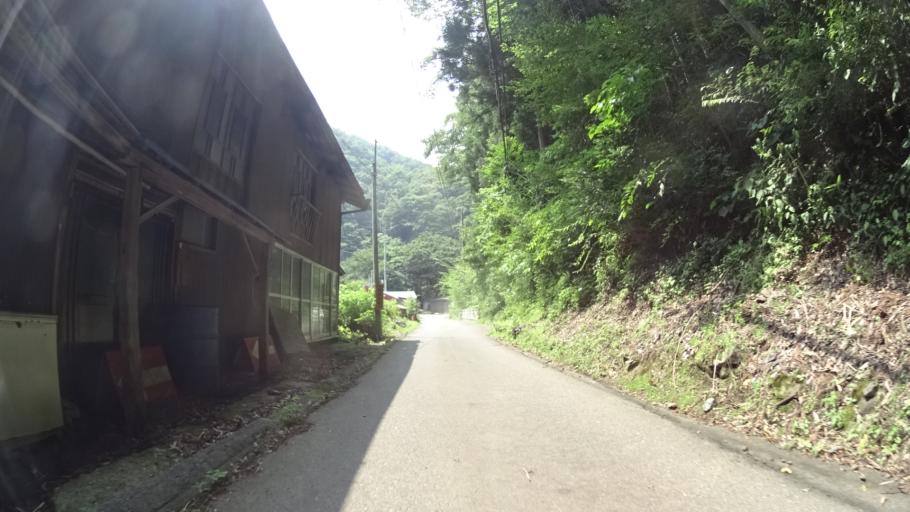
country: JP
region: Gunma
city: Tomioka
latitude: 36.0837
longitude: 138.7191
